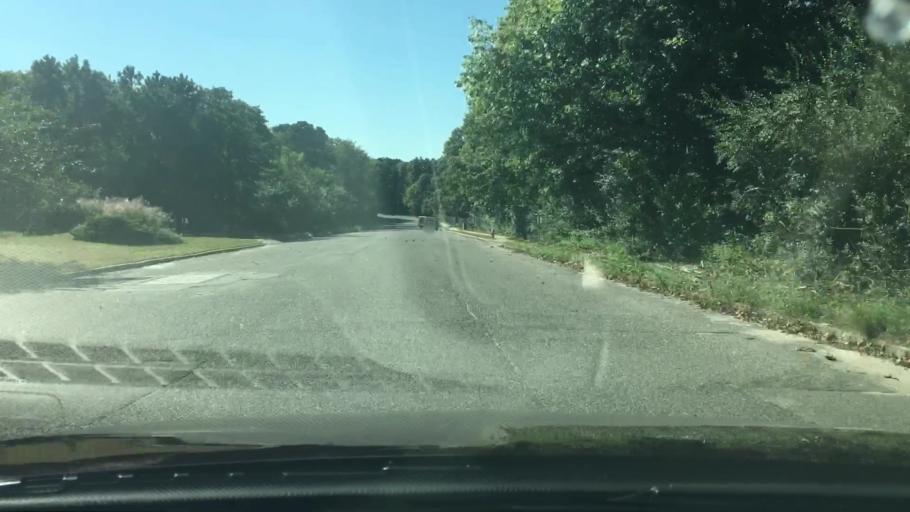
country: US
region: New York
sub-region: Suffolk County
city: Yaphank
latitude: 40.8453
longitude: -72.8828
